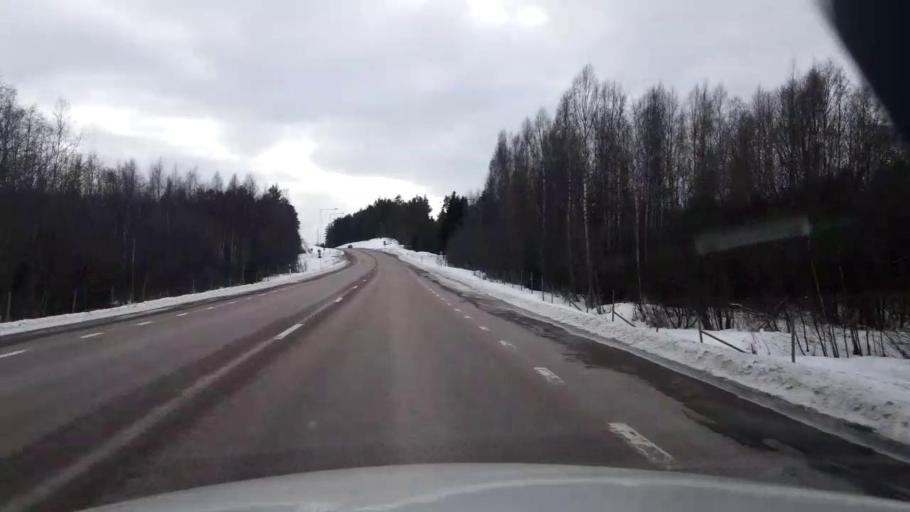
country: SE
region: Gaevleborg
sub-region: Nordanstigs Kommun
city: Bergsjoe
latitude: 61.9919
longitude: 17.2405
